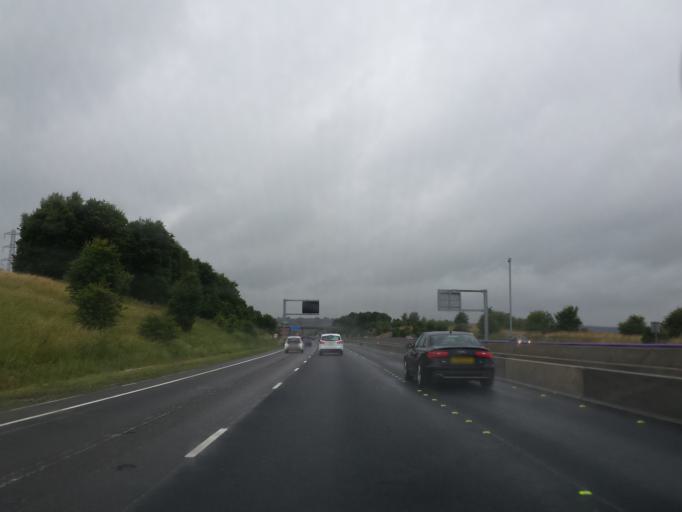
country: GB
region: England
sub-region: Derbyshire
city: Staveley
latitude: 53.2600
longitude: -1.3146
